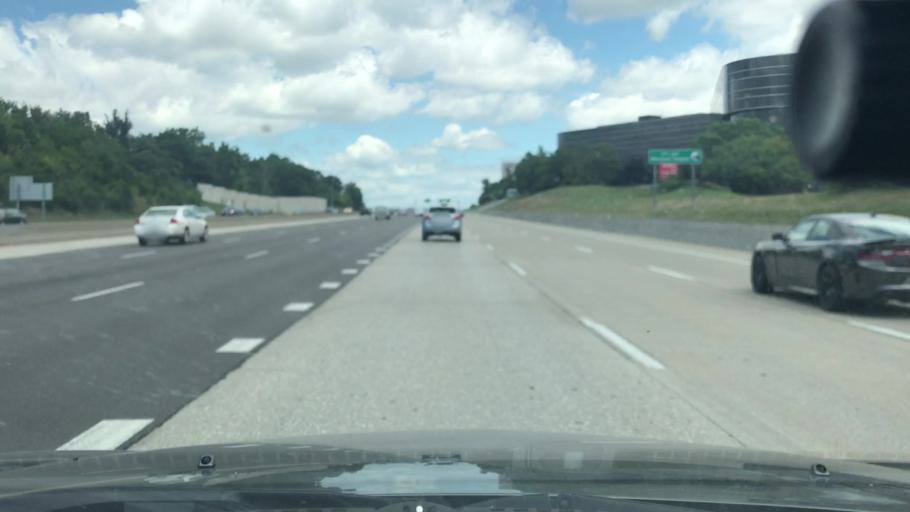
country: US
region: Missouri
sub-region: Saint Louis County
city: Maryland Heights
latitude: 38.6880
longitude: -90.4499
